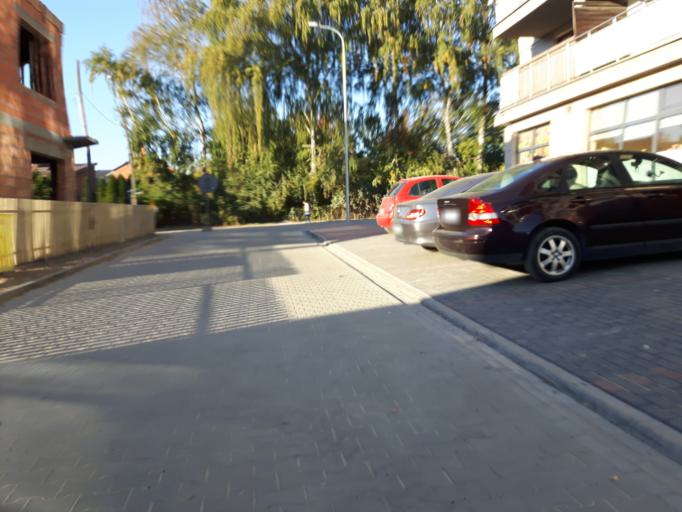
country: PL
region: Masovian Voivodeship
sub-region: Powiat wolominski
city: Zabki
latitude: 52.2818
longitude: 21.1295
